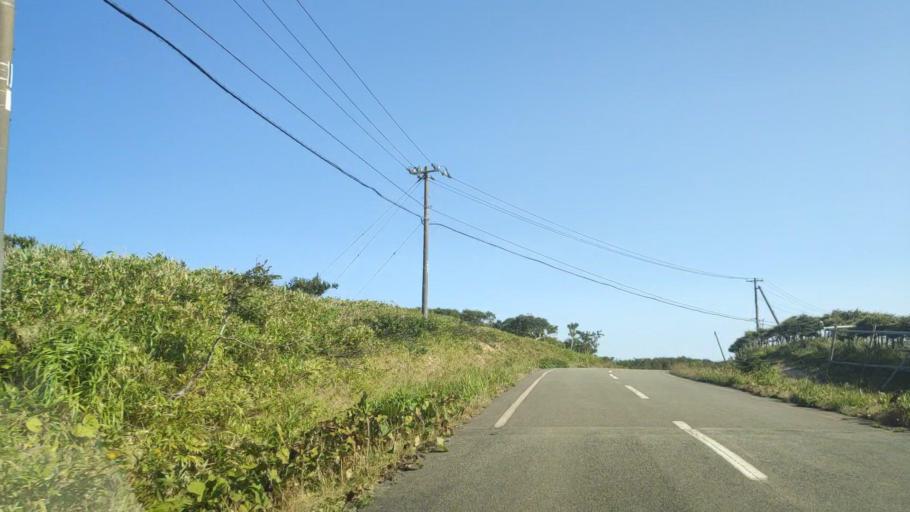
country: JP
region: Hokkaido
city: Wakkanai
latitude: 45.4158
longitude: 141.6624
